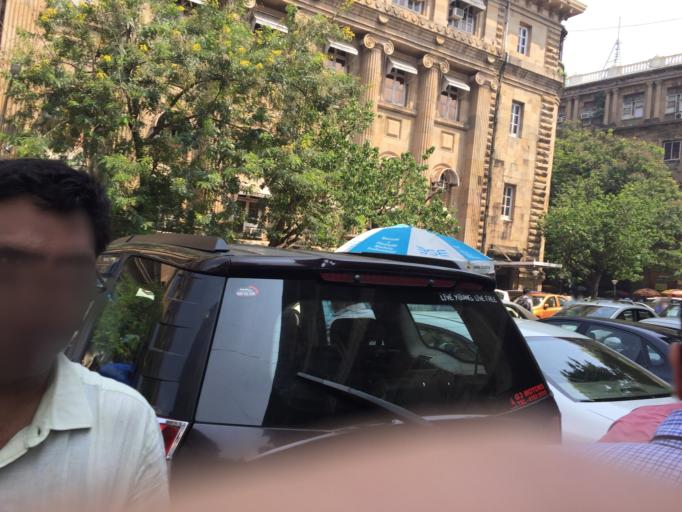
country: IN
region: Maharashtra
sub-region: Raigarh
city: Uran
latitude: 18.9312
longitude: 72.8341
